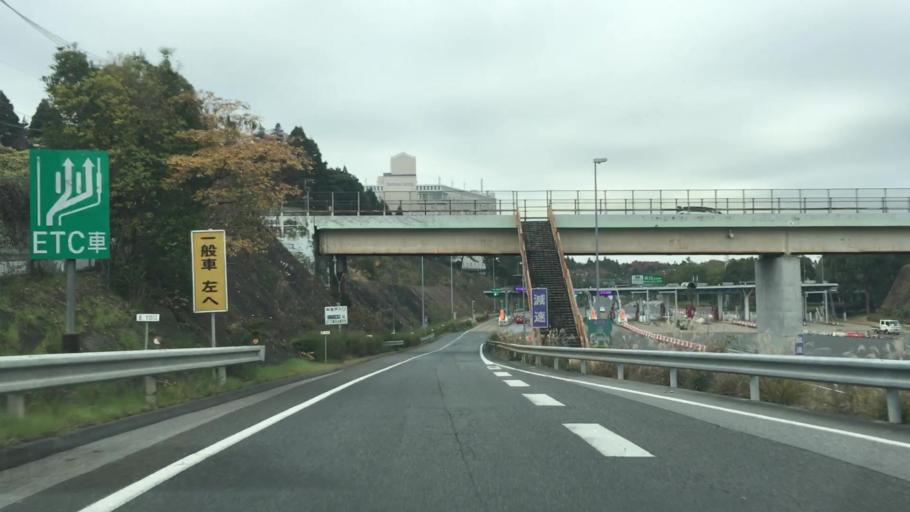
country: JP
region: Chiba
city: Narita
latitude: 35.7817
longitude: 140.3528
